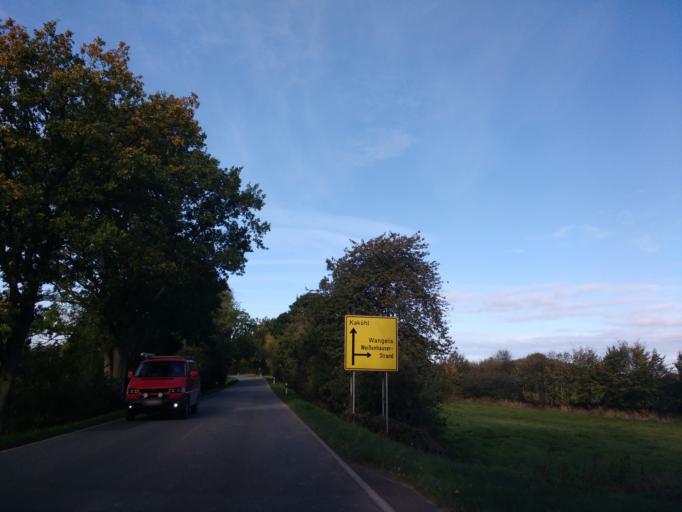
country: DE
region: Schleswig-Holstein
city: Wangels
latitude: 54.2579
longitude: 10.7470
